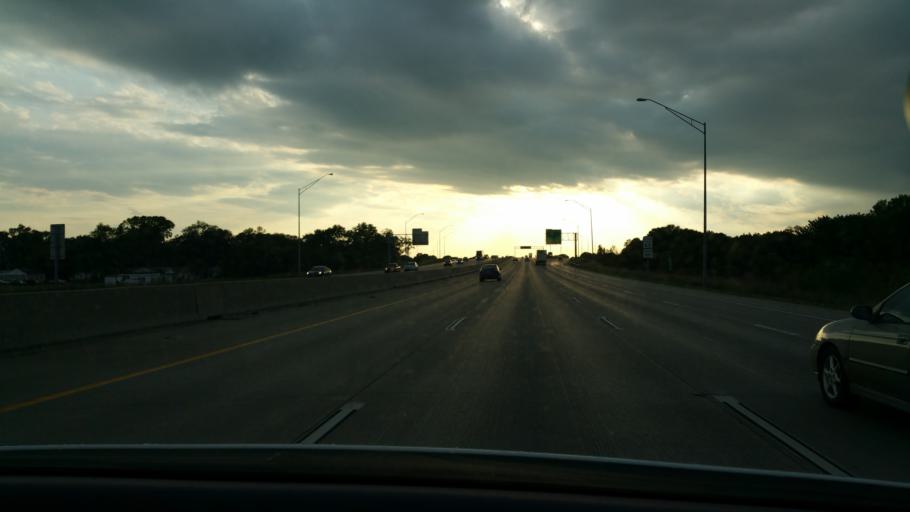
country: US
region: Iowa
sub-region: Polk County
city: Saylorville
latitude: 41.6495
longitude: -93.6095
